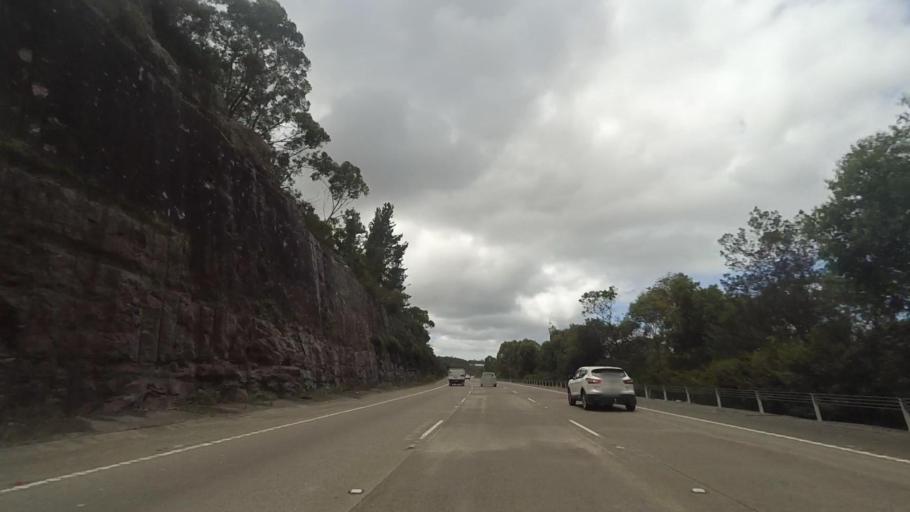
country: AU
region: New South Wales
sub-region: Gosford Shire
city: Point Clare
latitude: -33.4323
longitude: 151.2708
